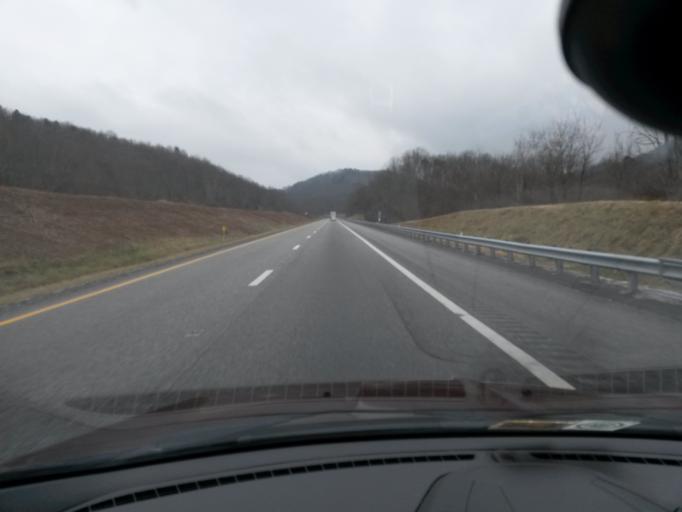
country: US
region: Virginia
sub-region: City of Lexington
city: Lexington
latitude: 37.8785
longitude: -79.6073
